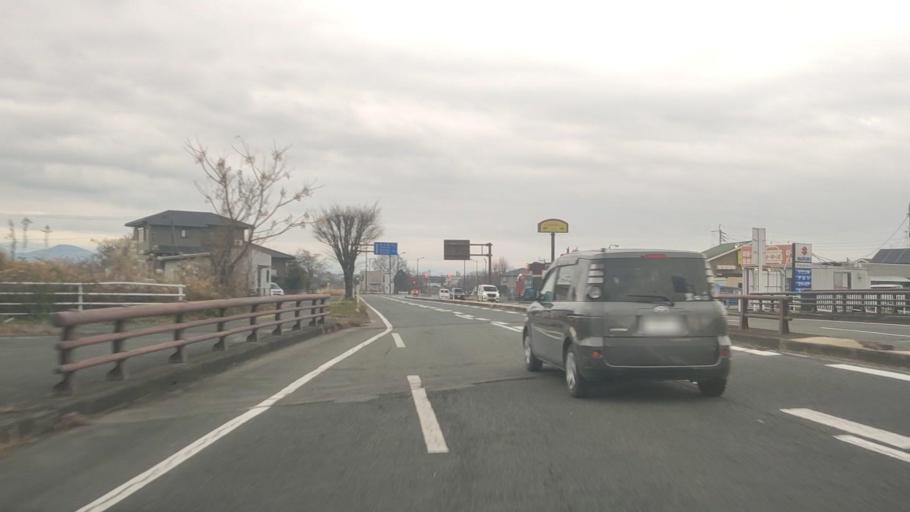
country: JP
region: Kumamoto
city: Ozu
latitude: 32.8237
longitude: 130.7911
